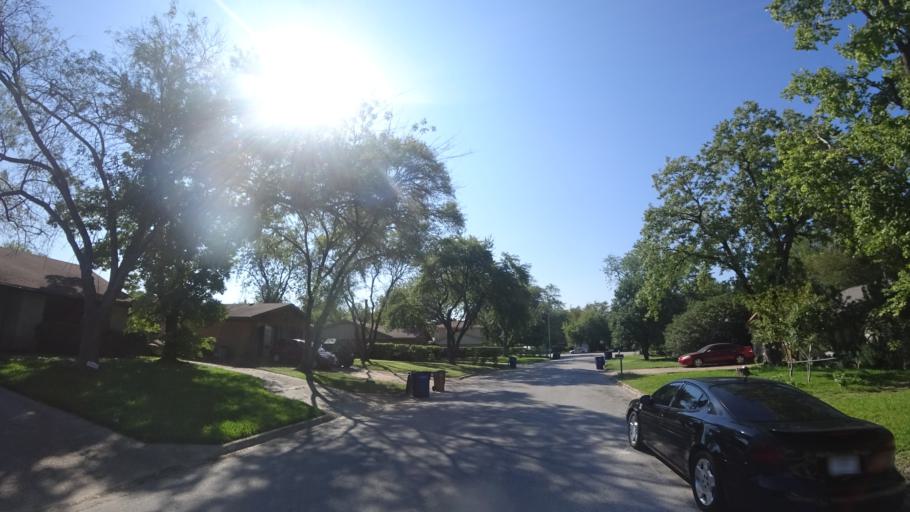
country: US
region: Texas
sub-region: Travis County
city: Austin
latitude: 30.3185
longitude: -97.6680
